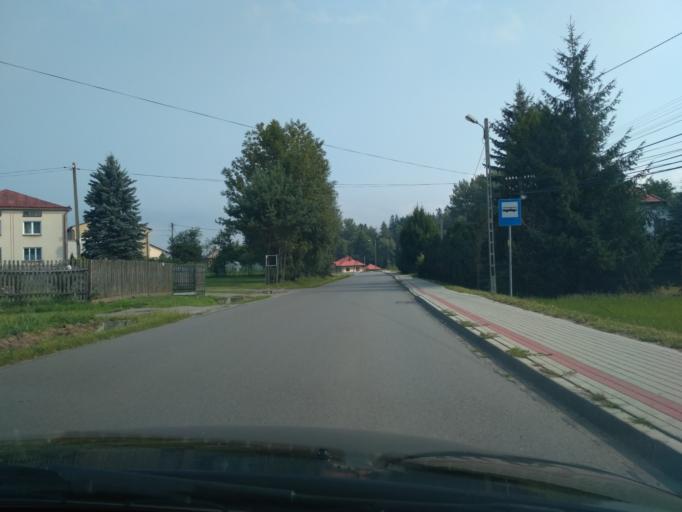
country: PL
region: Subcarpathian Voivodeship
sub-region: Powiat rzeszowski
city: Niechobrz
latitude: 49.9896
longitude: 21.8758
